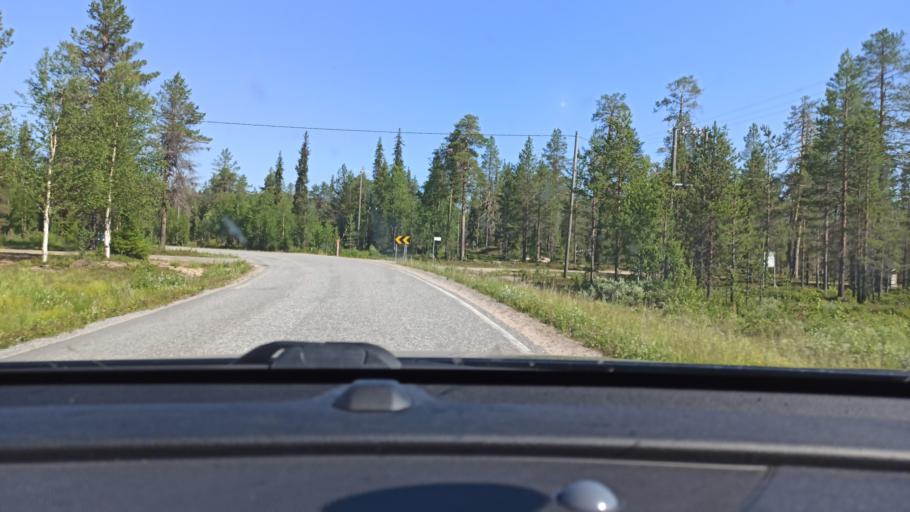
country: FI
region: Lapland
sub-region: Tunturi-Lappi
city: Kolari
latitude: 67.6332
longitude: 24.1600
